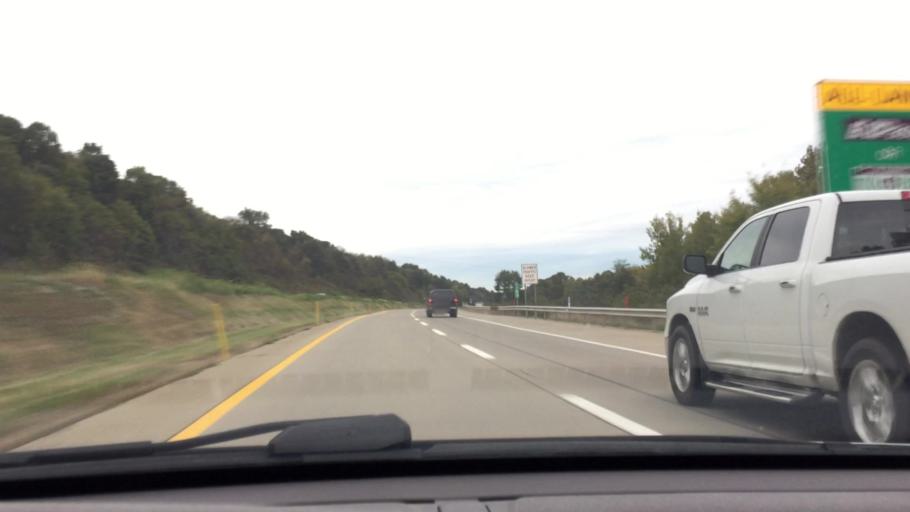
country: US
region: Pennsylvania
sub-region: Lawrence County
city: New Beaver
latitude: 40.9329
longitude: -80.3909
